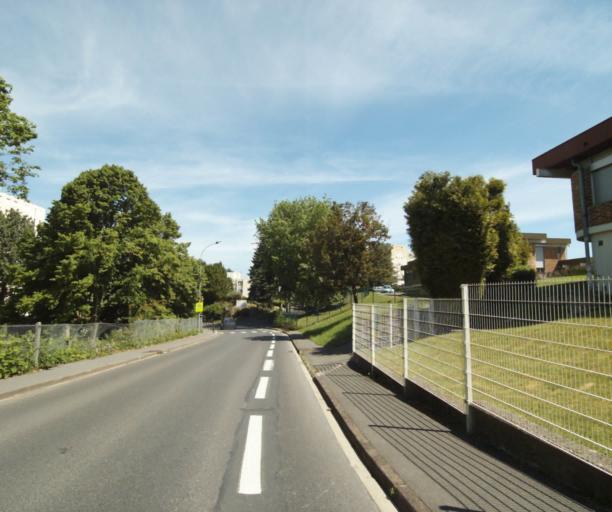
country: FR
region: Champagne-Ardenne
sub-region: Departement des Ardennes
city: La Francheville
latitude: 49.7440
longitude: 4.7212
